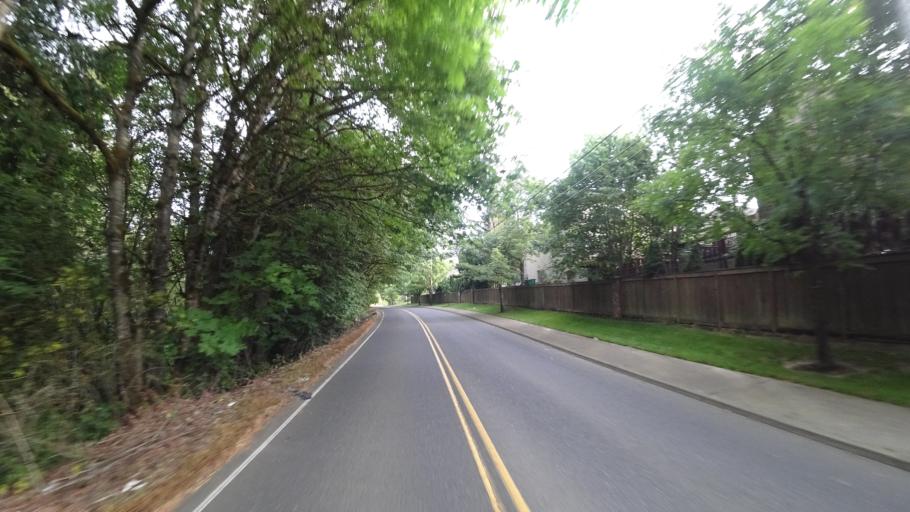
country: US
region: Oregon
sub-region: Clackamas County
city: Happy Valley
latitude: 45.4717
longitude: -122.4971
